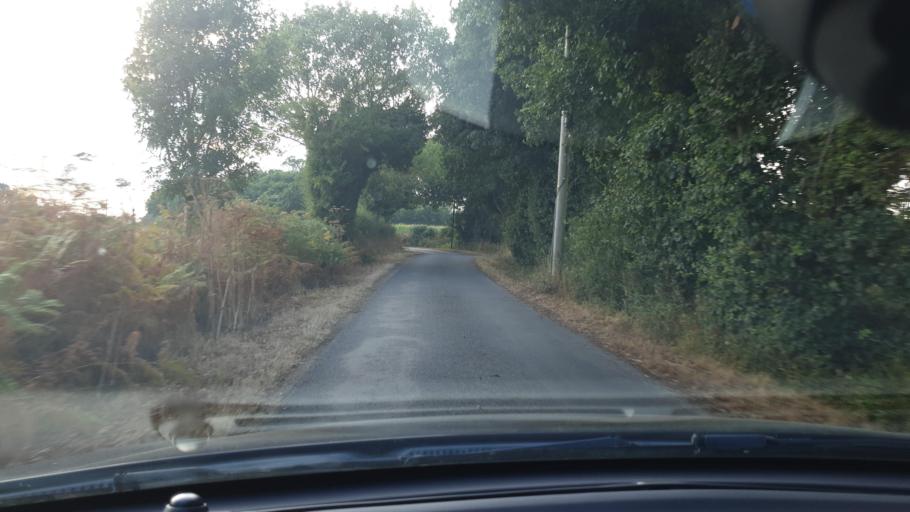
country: GB
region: England
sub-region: Essex
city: Alresford
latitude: 51.9077
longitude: 1.0173
